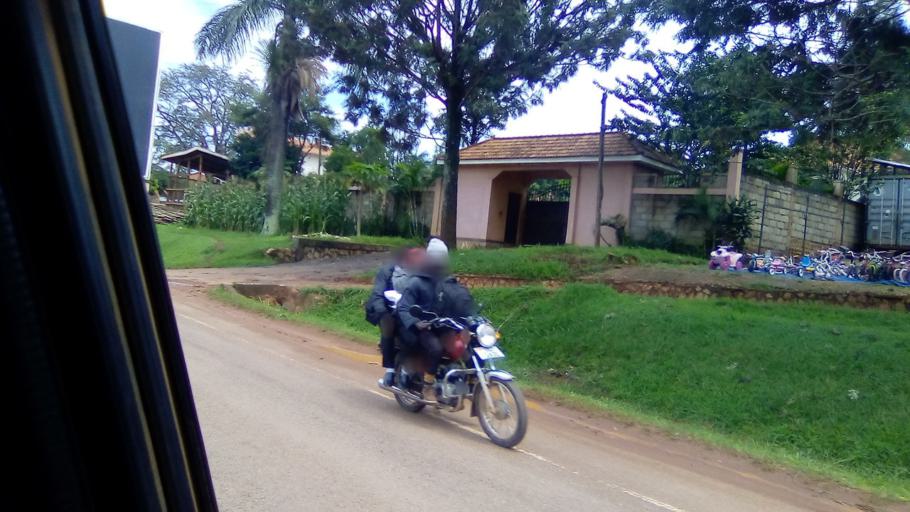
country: UG
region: Central Region
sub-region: Wakiso District
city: Kajansi
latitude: 0.1685
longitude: 32.5428
